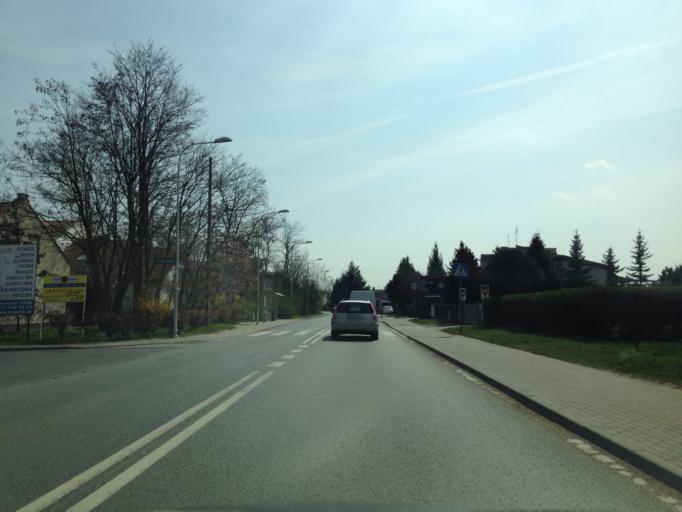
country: PL
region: Lower Silesian Voivodeship
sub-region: Powiat wroclawski
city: Wilczyce
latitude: 51.1117
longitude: 17.1364
